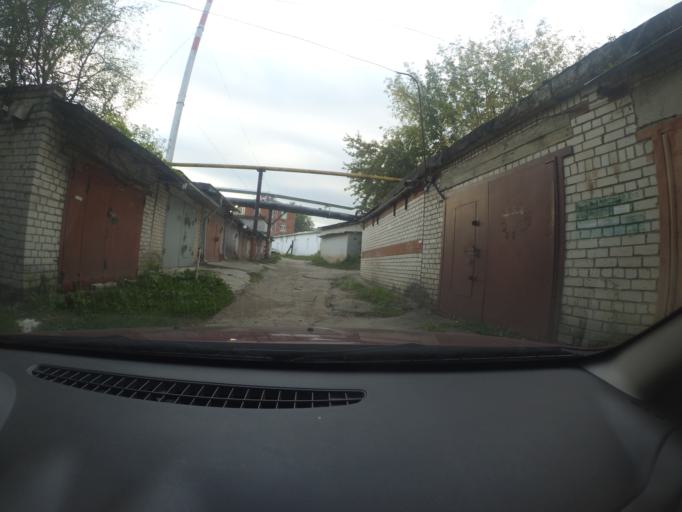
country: RU
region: Nizjnij Novgorod
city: Nizhniy Novgorod
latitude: 56.2802
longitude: 43.9851
